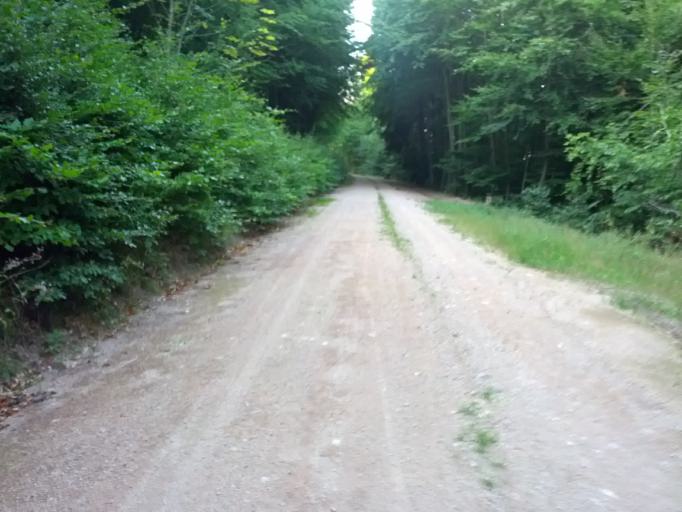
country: DE
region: Thuringia
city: Eisenach
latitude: 50.9472
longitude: 10.3394
